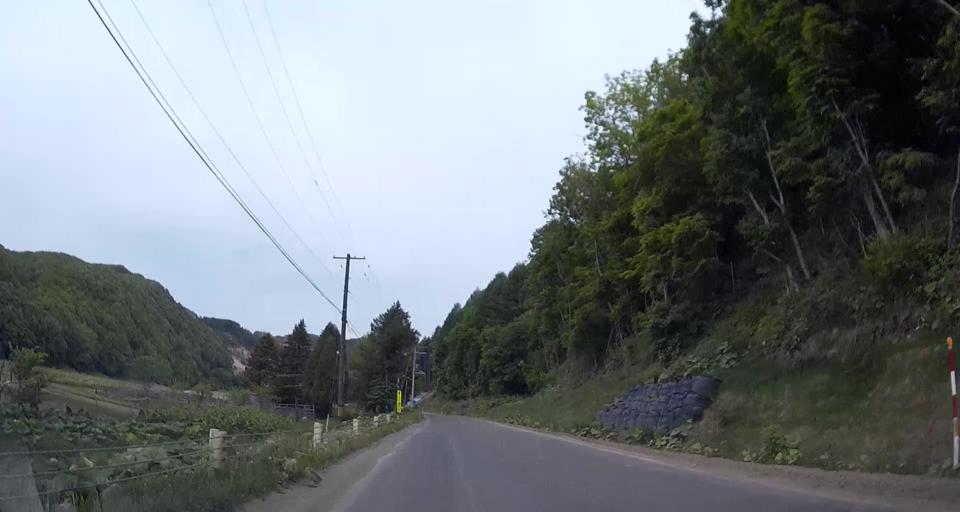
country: JP
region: Hokkaido
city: Chitose
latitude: 42.7580
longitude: 141.9791
